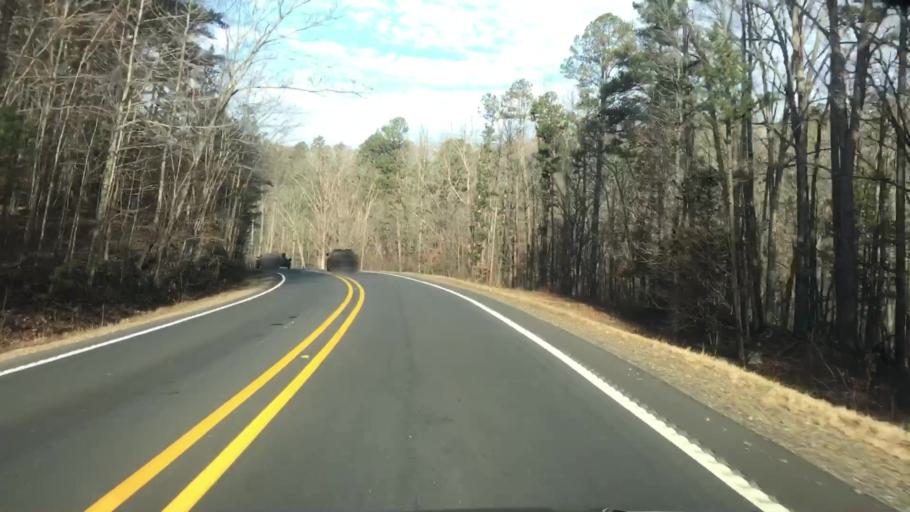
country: US
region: Arkansas
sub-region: Montgomery County
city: Mount Ida
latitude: 34.5240
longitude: -93.4008
